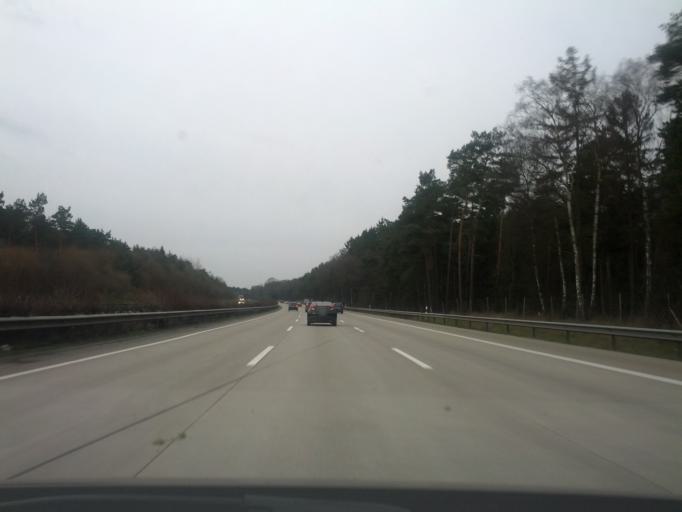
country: DE
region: Lower Saxony
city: Bispingen
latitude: 53.1416
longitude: 10.0059
